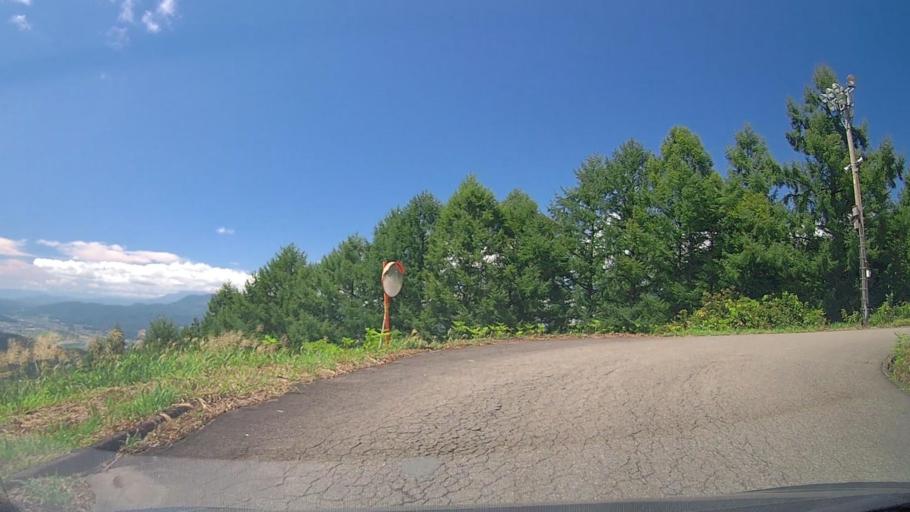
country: JP
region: Nagano
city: Iiyama
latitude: 36.9333
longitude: 138.4561
